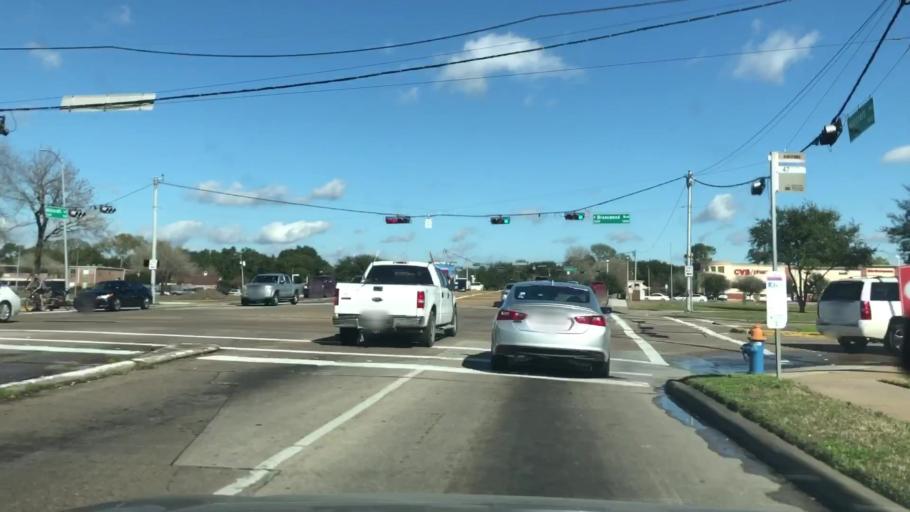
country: US
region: Texas
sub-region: Harris County
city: Bellaire
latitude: 29.6774
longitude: -95.4935
